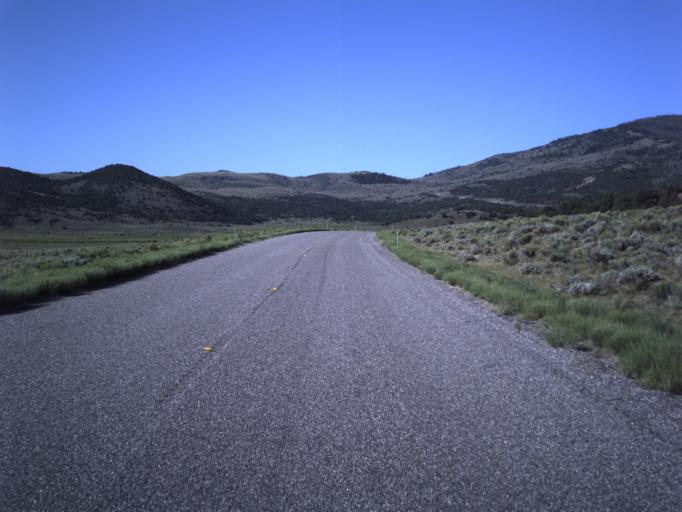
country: US
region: Utah
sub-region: Wayne County
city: Loa
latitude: 38.6308
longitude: -111.4446
